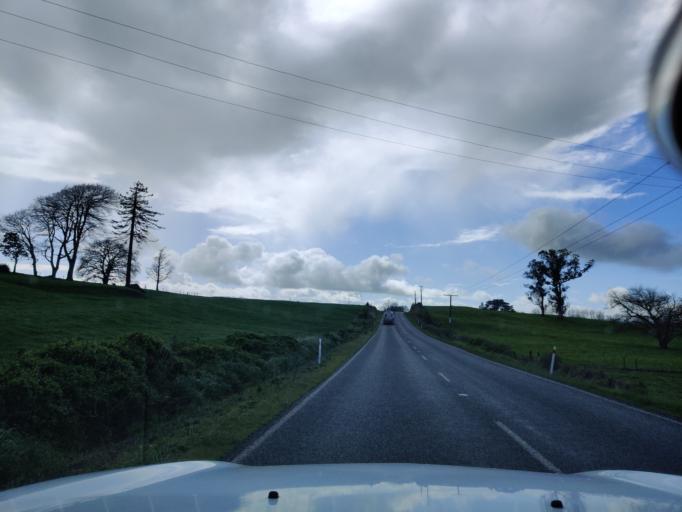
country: NZ
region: Waikato
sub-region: Waikato District
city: Ngaruawahia
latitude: -37.5750
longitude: 175.2400
